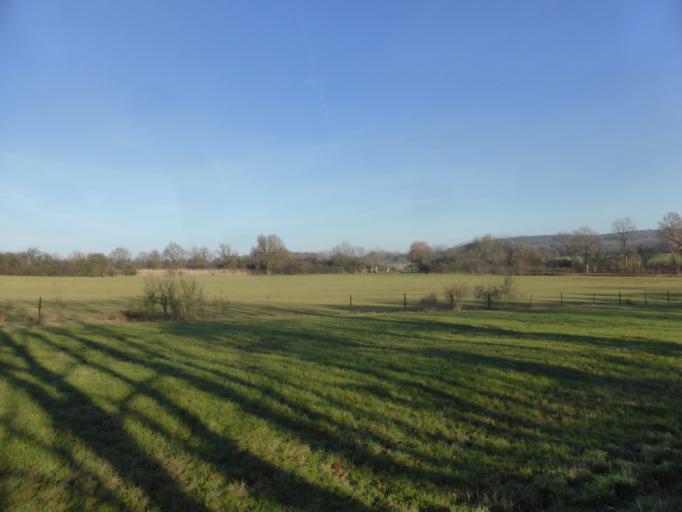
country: LU
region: Luxembourg
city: Hautcharage
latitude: 49.5897
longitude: 5.9068
